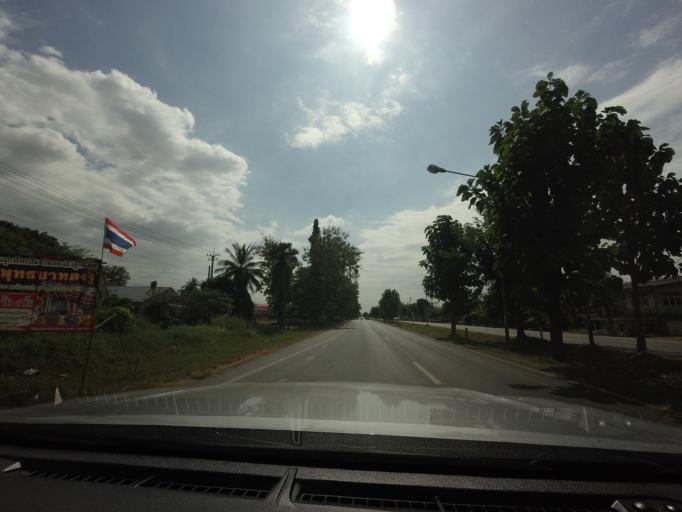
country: TH
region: Phitsanulok
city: Wang Thong
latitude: 16.7470
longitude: 100.4320
